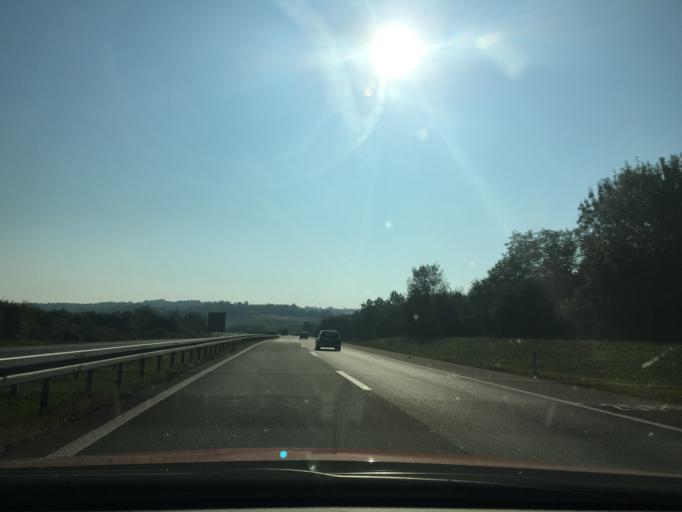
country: RS
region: Central Serbia
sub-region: Podunavski Okrug
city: Smederevo
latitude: 44.5741
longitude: 20.9086
